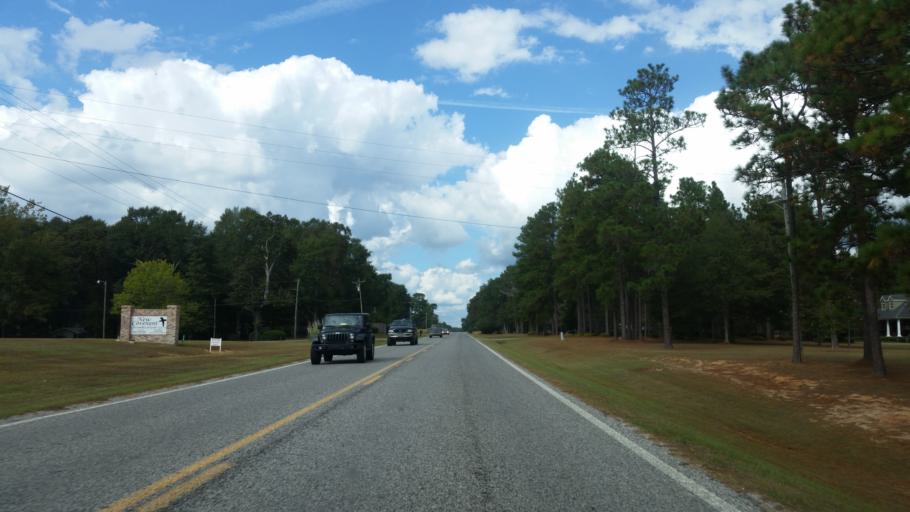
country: US
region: Mississippi
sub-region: Stone County
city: Wiggins
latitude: 30.8816
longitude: -89.1169
